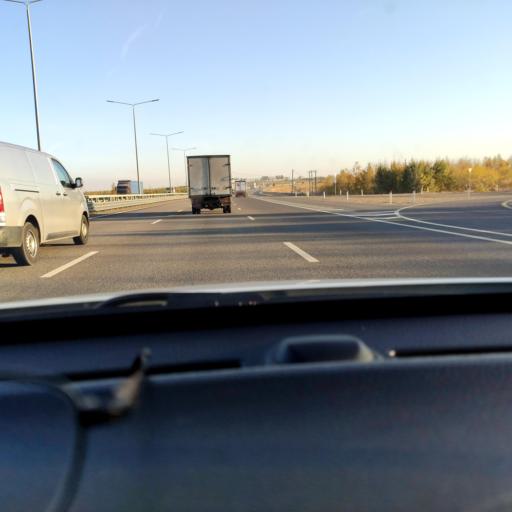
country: RU
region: Voronezj
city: Somovo
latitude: 51.7783
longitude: 39.2973
